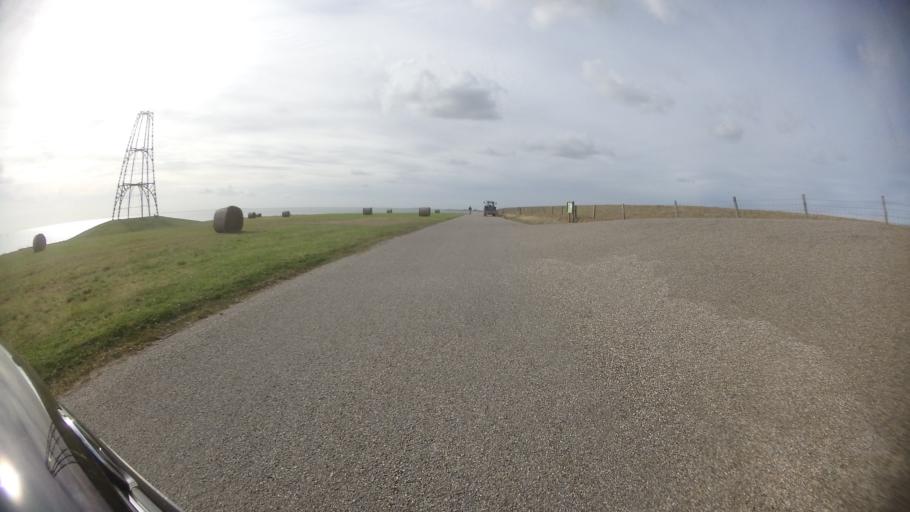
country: NL
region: North Holland
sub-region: Gemeente Texel
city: Den Burg
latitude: 53.0789
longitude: 4.8962
